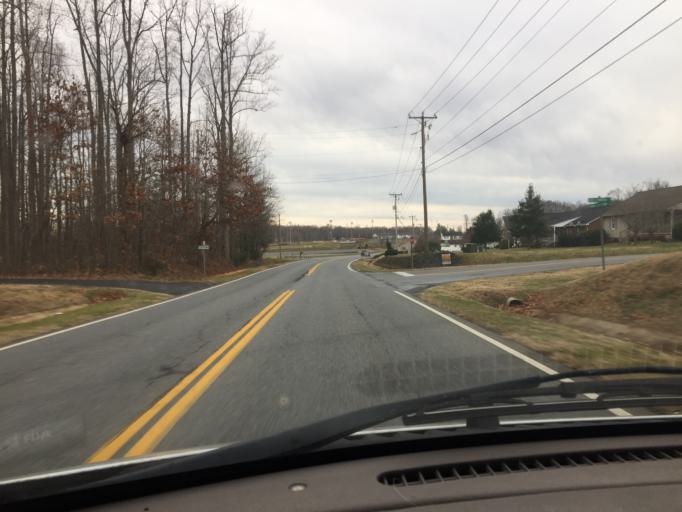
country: US
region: Virginia
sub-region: Bedford County
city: Forest
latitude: 37.3383
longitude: -79.2860
